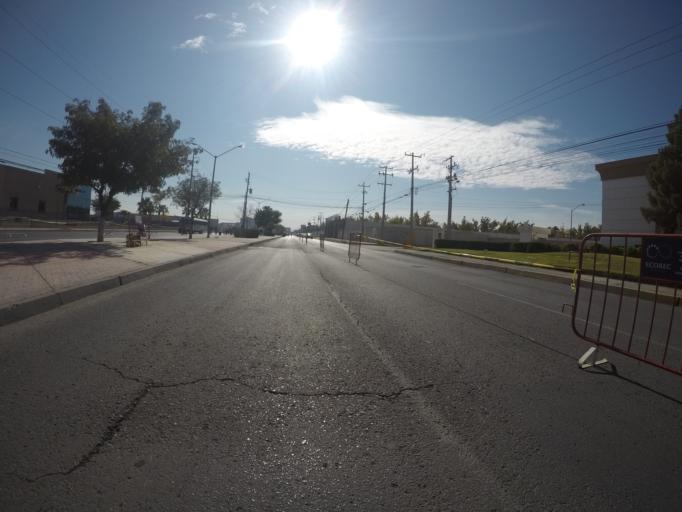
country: MX
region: Chihuahua
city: Ciudad Juarez
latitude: 31.7209
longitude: -106.3987
